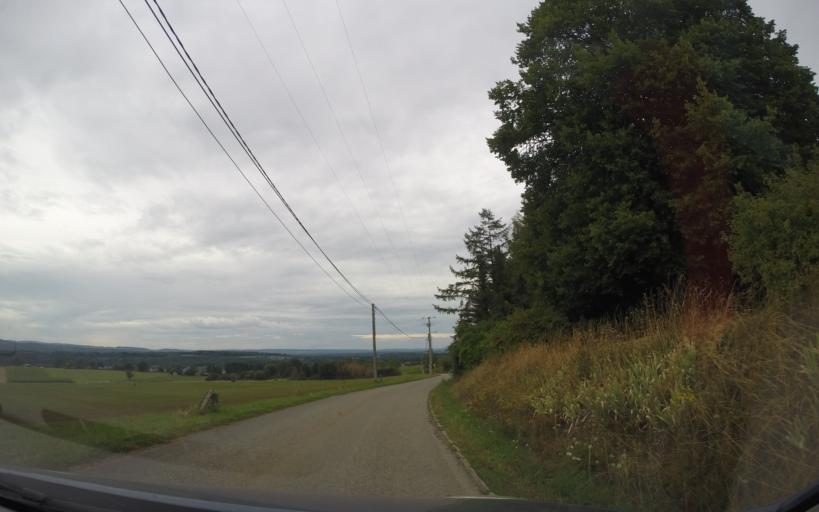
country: BE
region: Wallonia
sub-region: Province du Luxembourg
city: Durbuy
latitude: 50.3714
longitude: 5.4671
